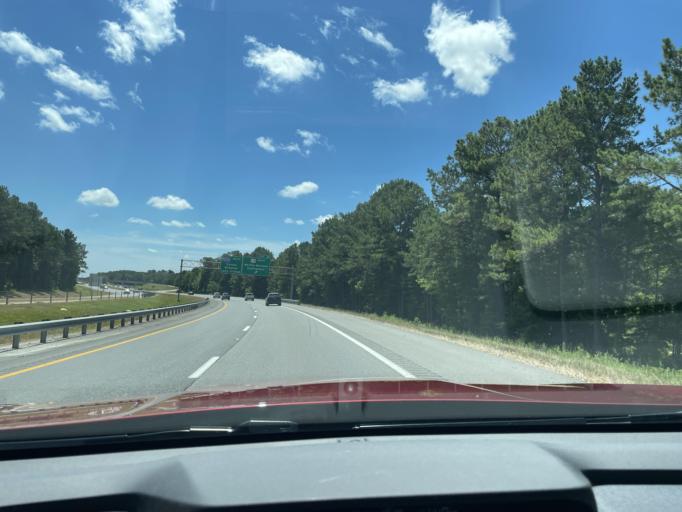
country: US
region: Arkansas
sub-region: Jefferson County
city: White Hall
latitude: 34.2481
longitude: -92.1006
